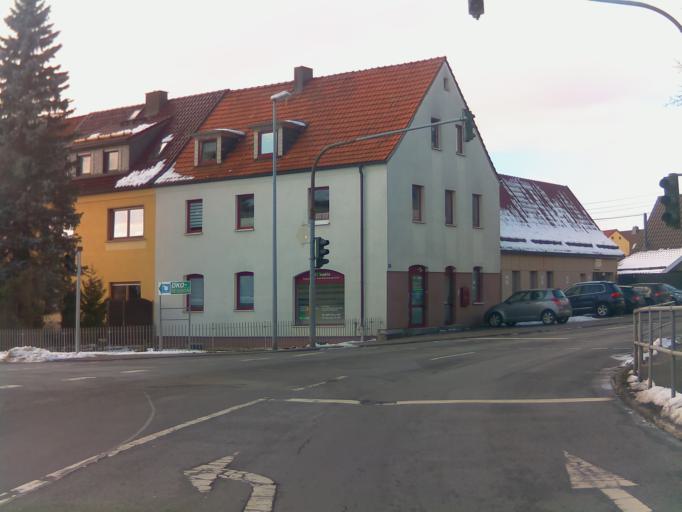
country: DE
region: Thuringia
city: Suhl
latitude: 50.6105
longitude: 10.6723
